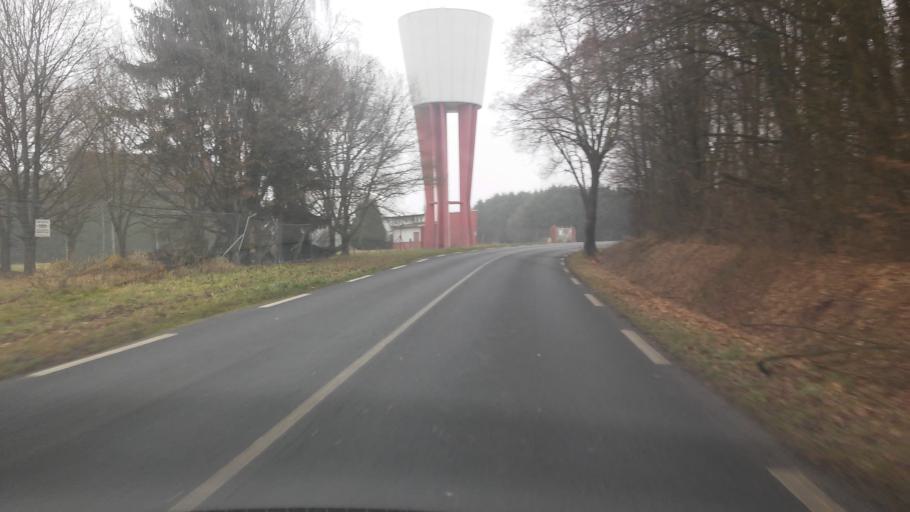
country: FR
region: Lorraine
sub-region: Departement de la Moselle
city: Augny
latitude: 49.0713
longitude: 6.1151
